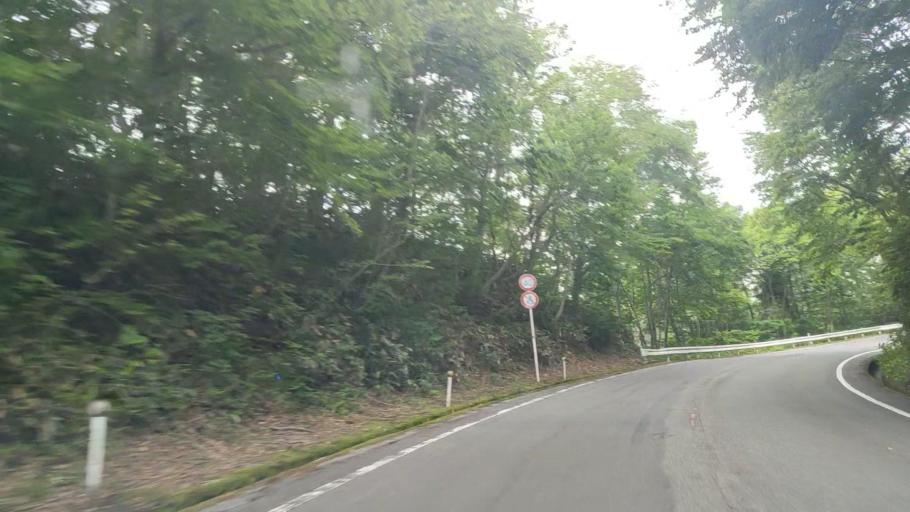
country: JP
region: Tottori
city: Kurayoshi
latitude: 35.3271
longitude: 133.5973
